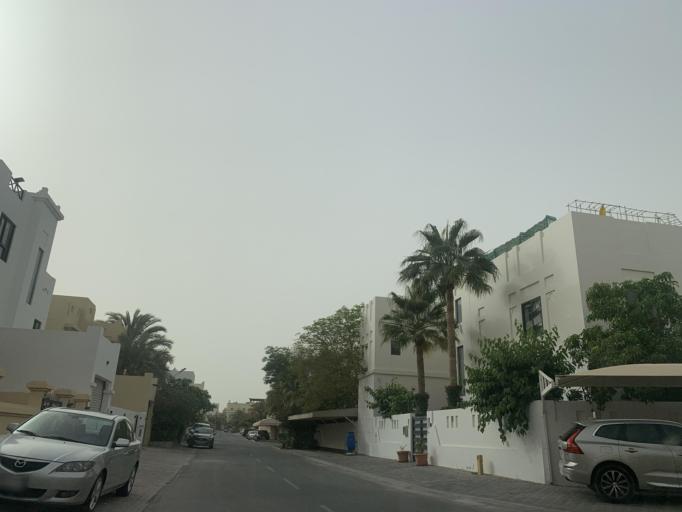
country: BH
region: Northern
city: Ar Rifa'
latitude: 26.1530
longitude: 50.5747
